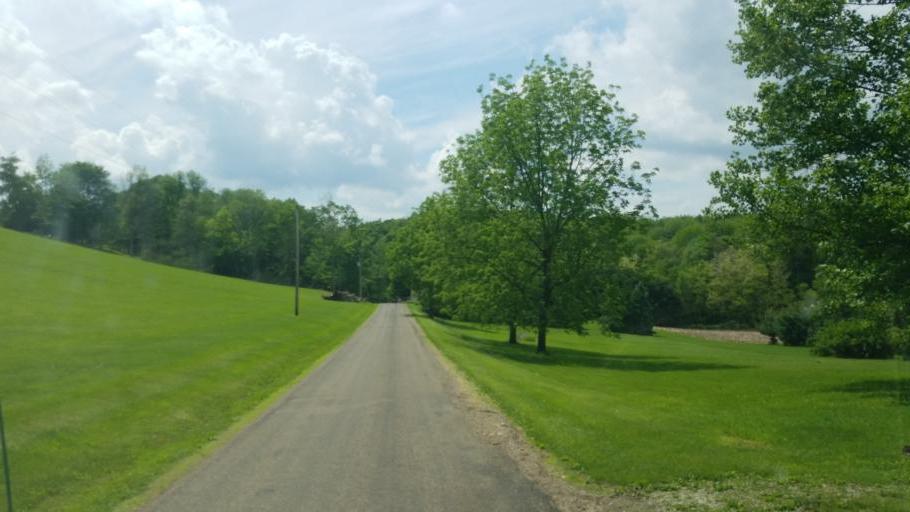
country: US
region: Ohio
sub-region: Sandusky County
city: Bellville
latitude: 40.6666
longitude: -82.3852
